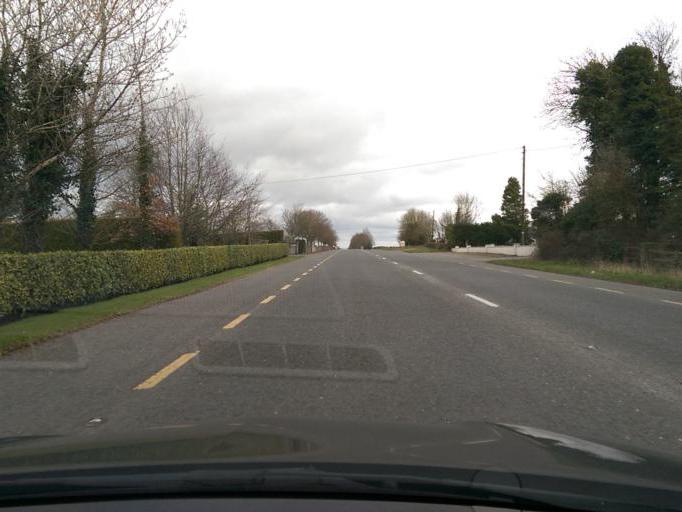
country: IE
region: Leinster
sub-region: An Iarmhi
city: Moate
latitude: 53.3940
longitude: -7.8336
